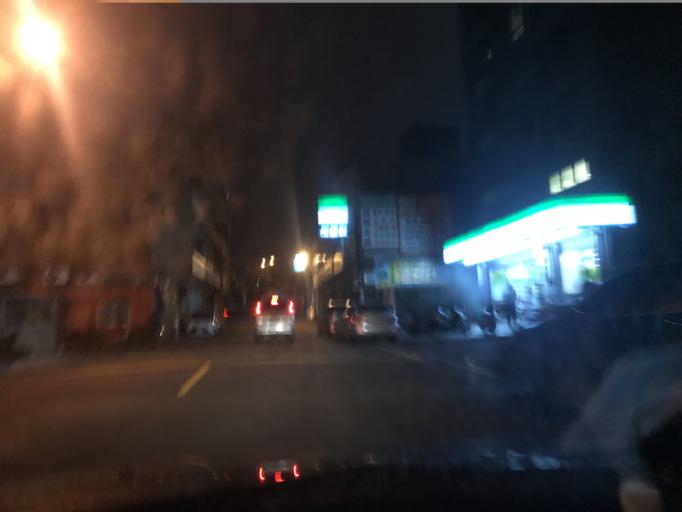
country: TW
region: Taiwan
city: Taoyuan City
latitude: 24.9653
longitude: 121.2364
